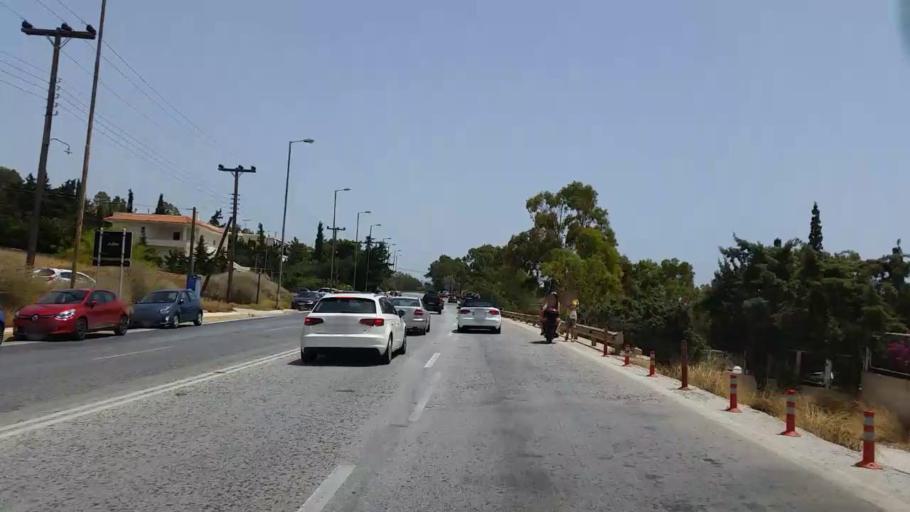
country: GR
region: Attica
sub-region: Nomarchia Anatolikis Attikis
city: Agios Dimitrios Kropias
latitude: 37.8084
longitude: 23.8482
